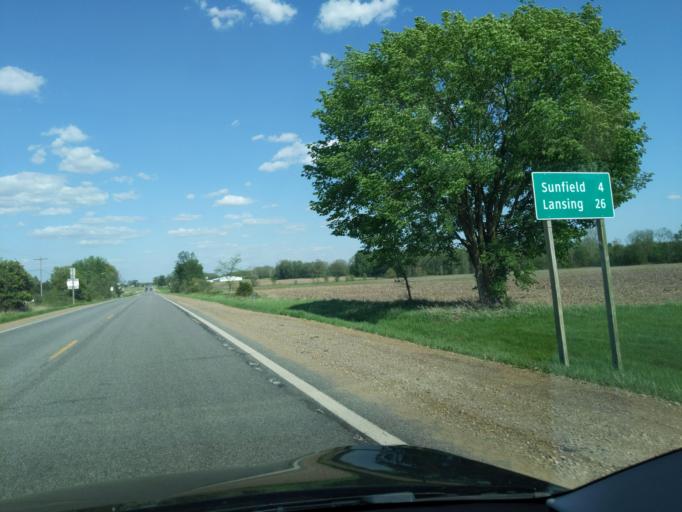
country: US
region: Michigan
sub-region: Ionia County
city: Lake Odessa
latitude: 42.7559
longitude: -85.0473
